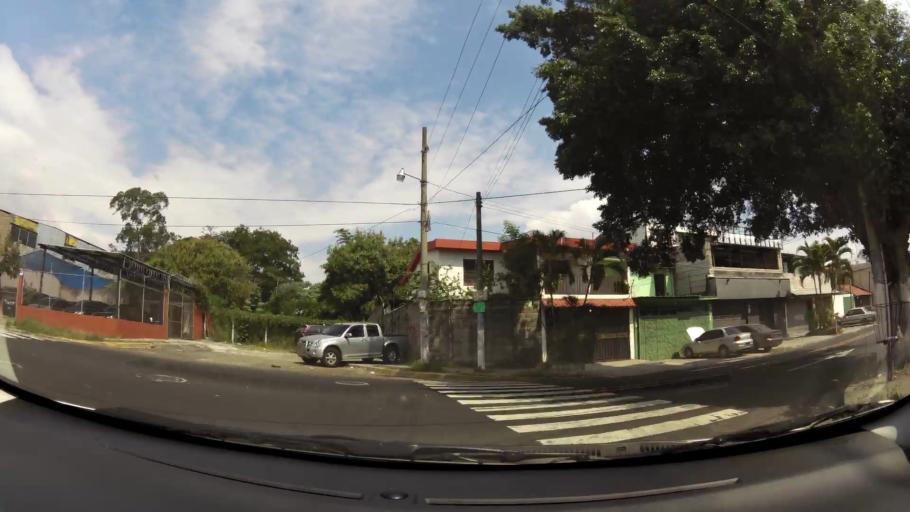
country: SV
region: San Salvador
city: Mejicanos
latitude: 13.7149
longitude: -89.2221
